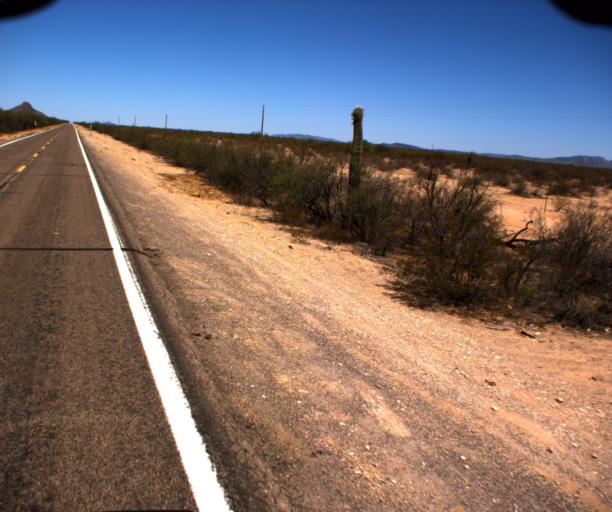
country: US
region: Arizona
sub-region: Pima County
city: Ajo
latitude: 32.1984
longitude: -112.4797
